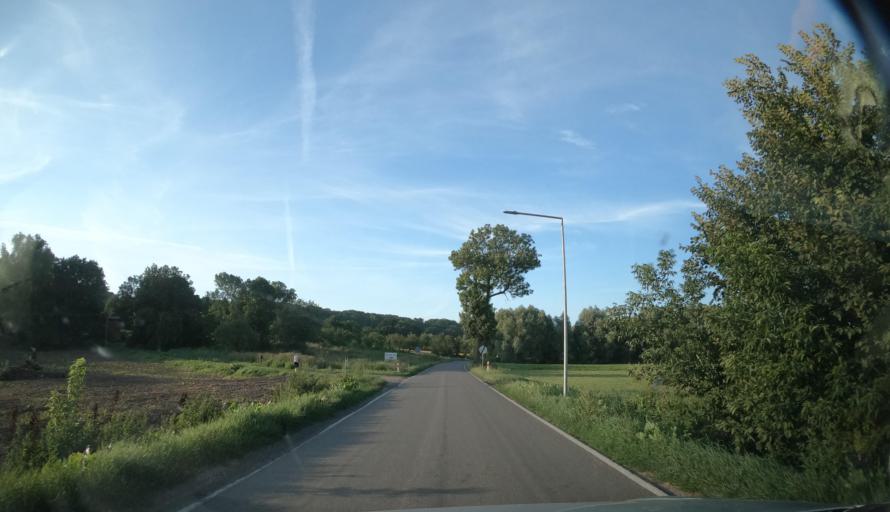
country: PL
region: Kujawsko-Pomorskie
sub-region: Bydgoszcz
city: Fordon
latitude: 53.2182
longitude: 18.1862
